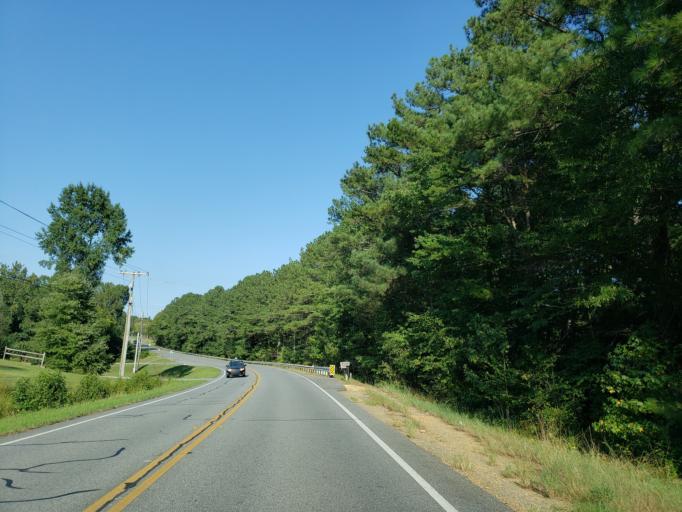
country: US
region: Georgia
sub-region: Whitfield County
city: Varnell
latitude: 34.9024
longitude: -84.8979
